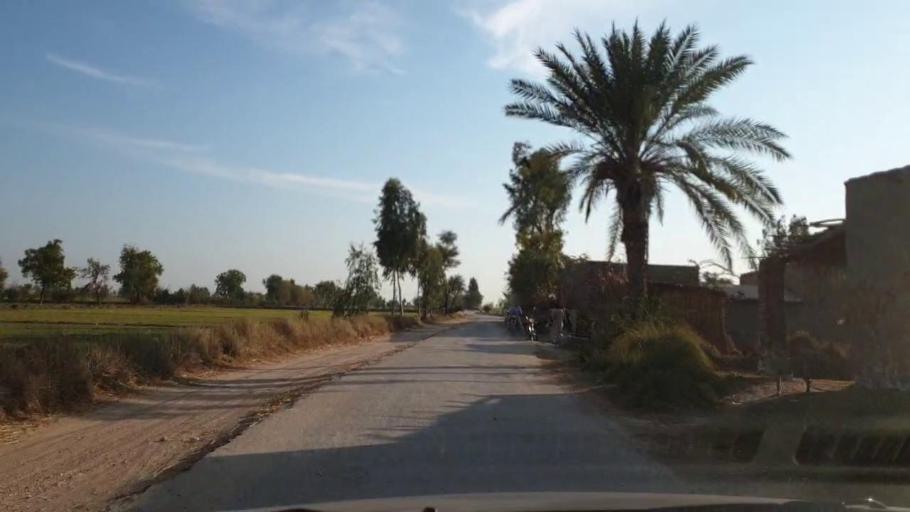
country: PK
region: Sindh
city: Khadro
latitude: 26.1890
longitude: 68.7498
